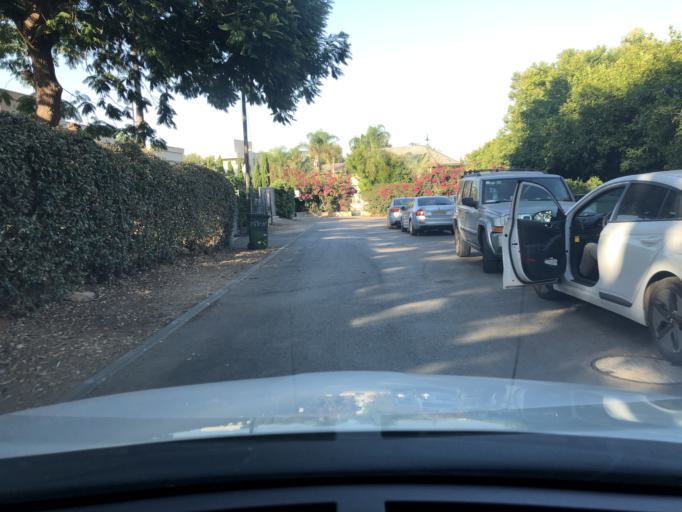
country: IL
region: Central District
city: Hod HaSharon
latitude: 32.1436
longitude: 34.9040
